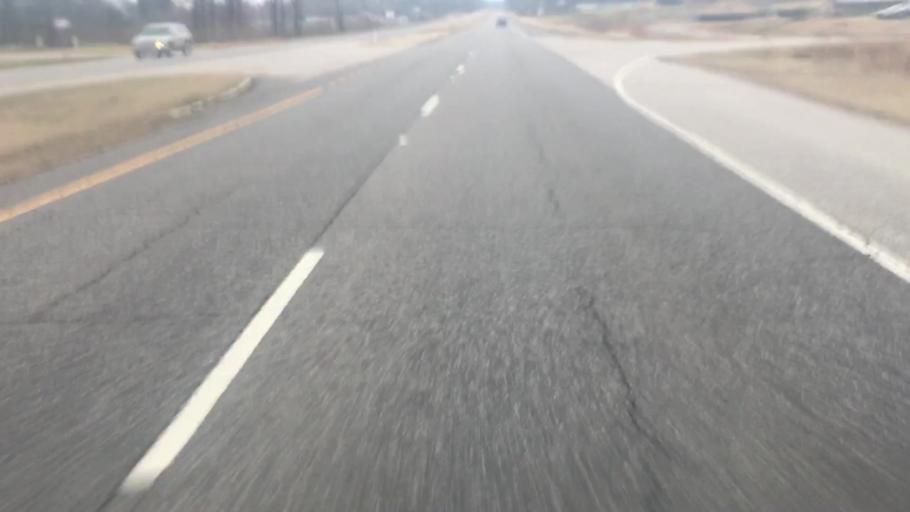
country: US
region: Alabama
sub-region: Walker County
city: Jasper
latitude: 33.8317
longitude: -87.2130
